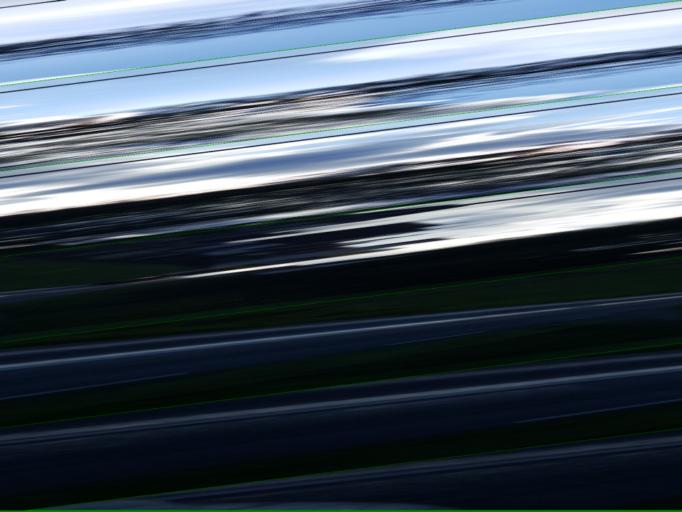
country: FR
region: Ile-de-France
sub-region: Departement du Val-d'Oise
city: Magny-en-Vexin
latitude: 49.1871
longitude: 1.8569
